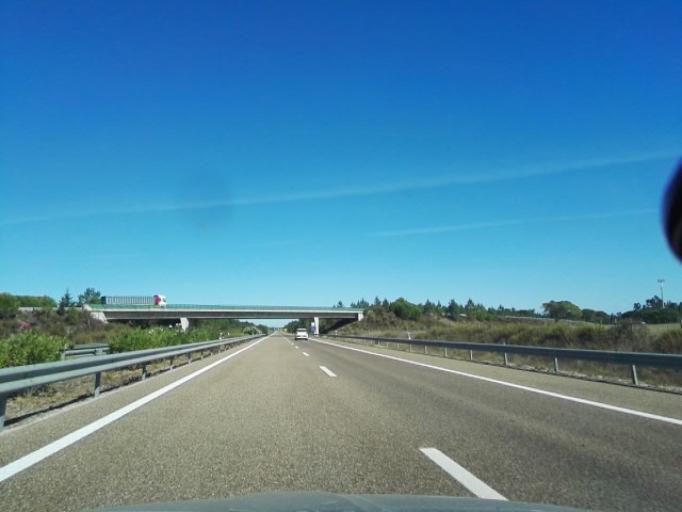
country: PT
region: Evora
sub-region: Vendas Novas
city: Vendas Novas
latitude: 38.6191
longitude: -8.6538
